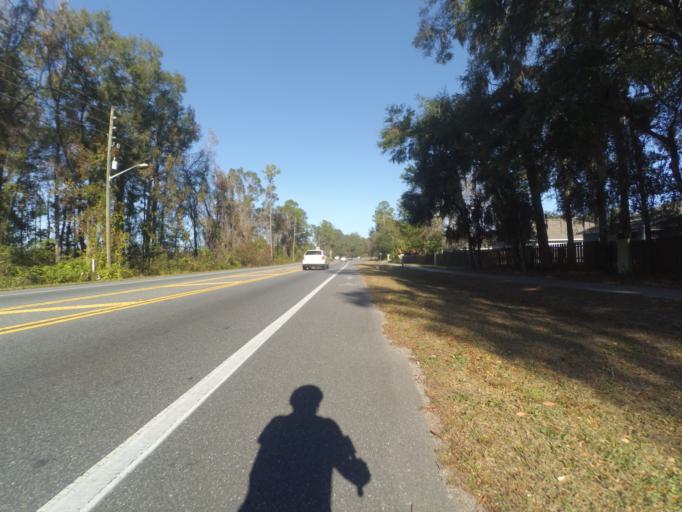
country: US
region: Florida
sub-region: Alachua County
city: Gainesville
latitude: 29.6362
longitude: -82.4134
